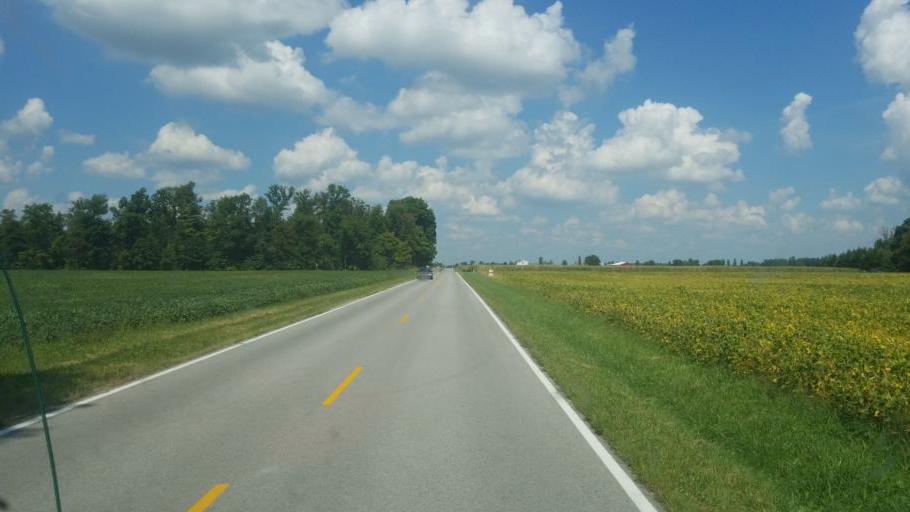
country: US
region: Ohio
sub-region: Hancock County
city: Arlington
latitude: 40.8685
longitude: -83.7273
